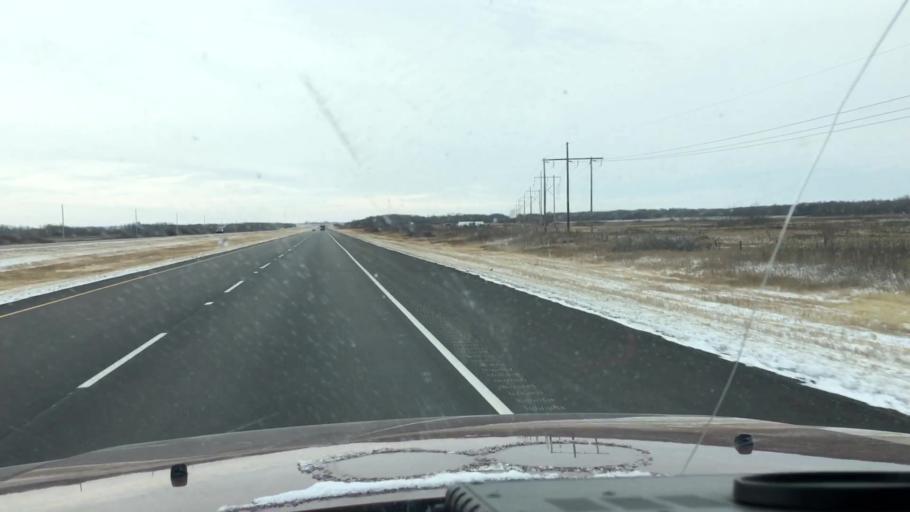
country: CA
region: Saskatchewan
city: Saskatoon
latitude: 51.8886
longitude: -106.5161
